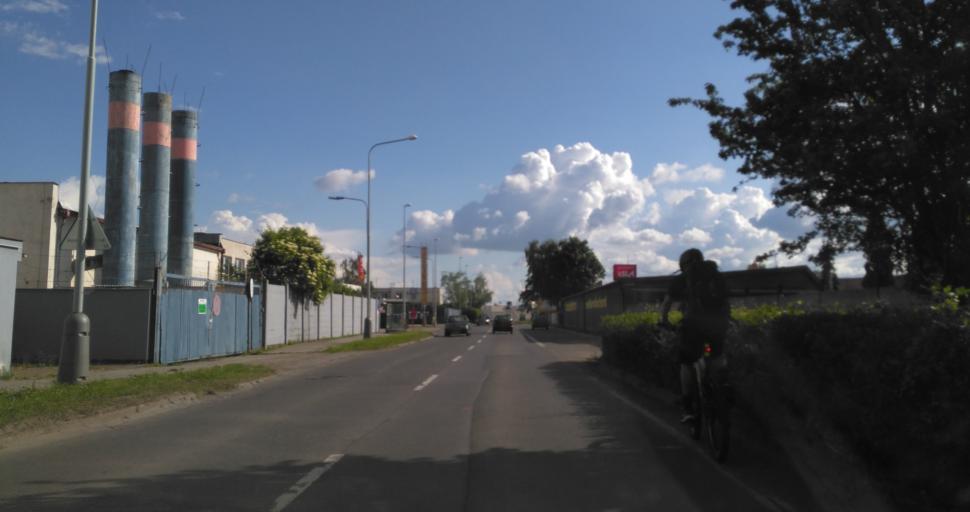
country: CZ
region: Praha
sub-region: Praha 19
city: Satalice
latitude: 50.1221
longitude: 14.5658
